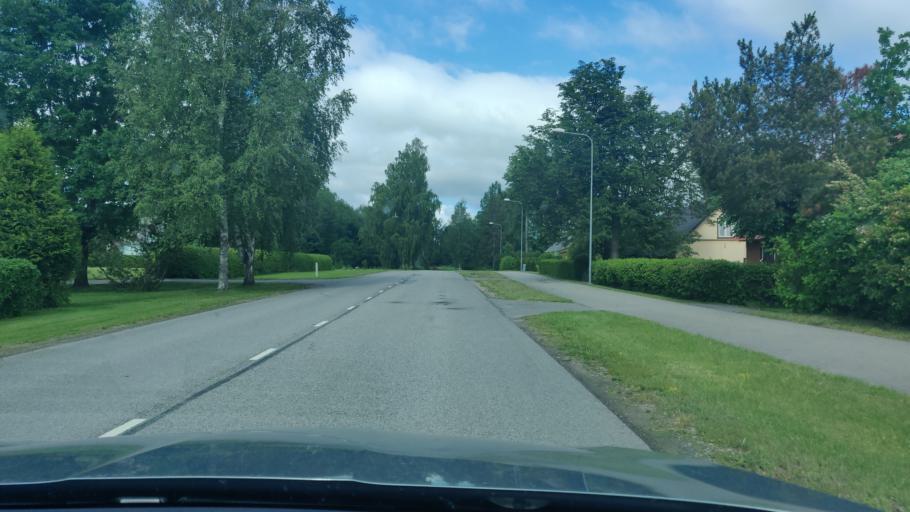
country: EE
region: Vorumaa
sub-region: Voru linn
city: Voru
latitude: 57.7287
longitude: 27.2975
